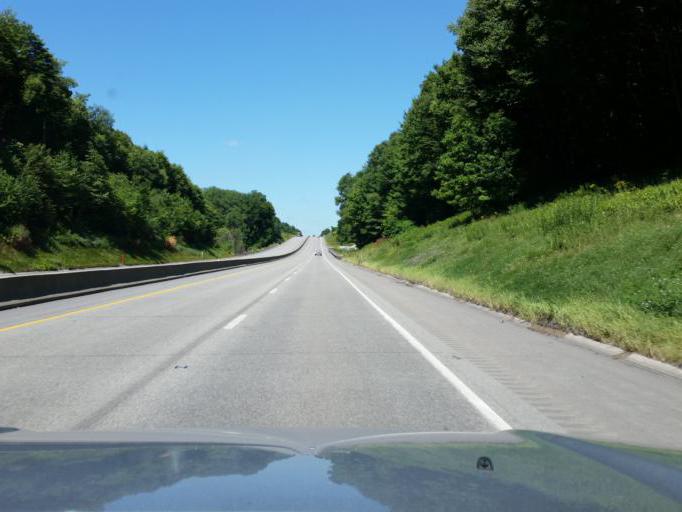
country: US
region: Pennsylvania
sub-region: Cambria County
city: Mundys Corner
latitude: 40.4474
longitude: -78.8115
